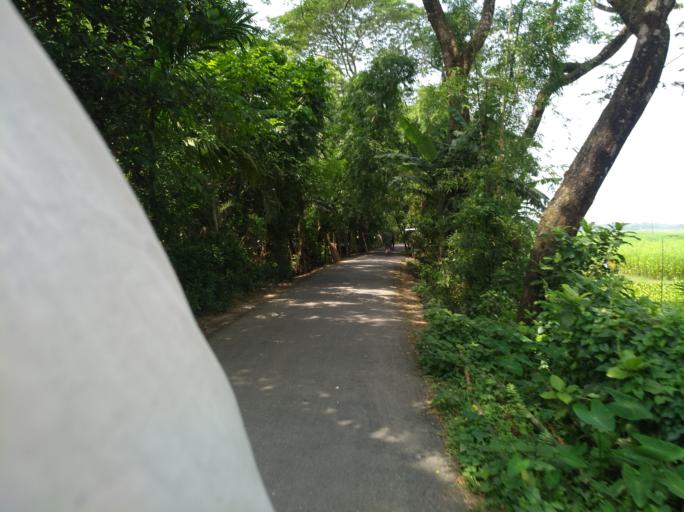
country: BD
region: Dhaka
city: Palang
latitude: 23.2513
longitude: 90.3103
